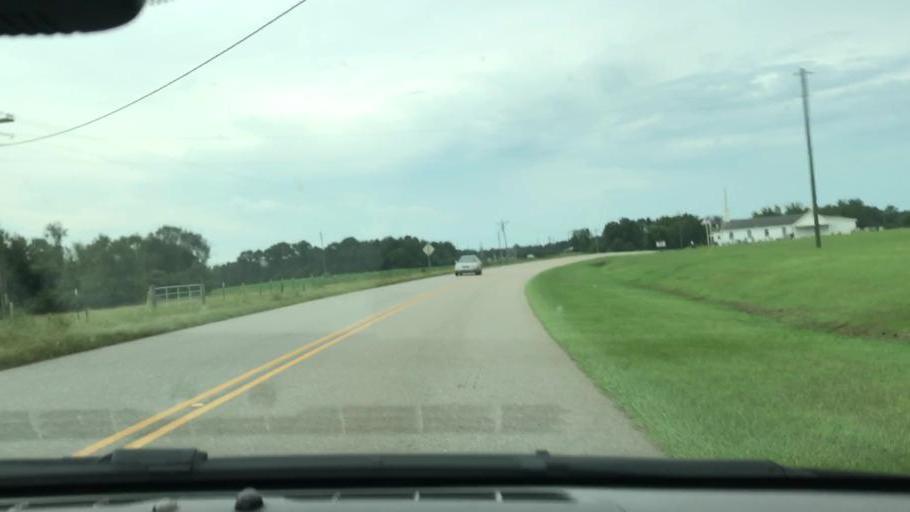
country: US
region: Alabama
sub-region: Houston County
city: Ashford
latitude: 31.2543
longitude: -85.1665
